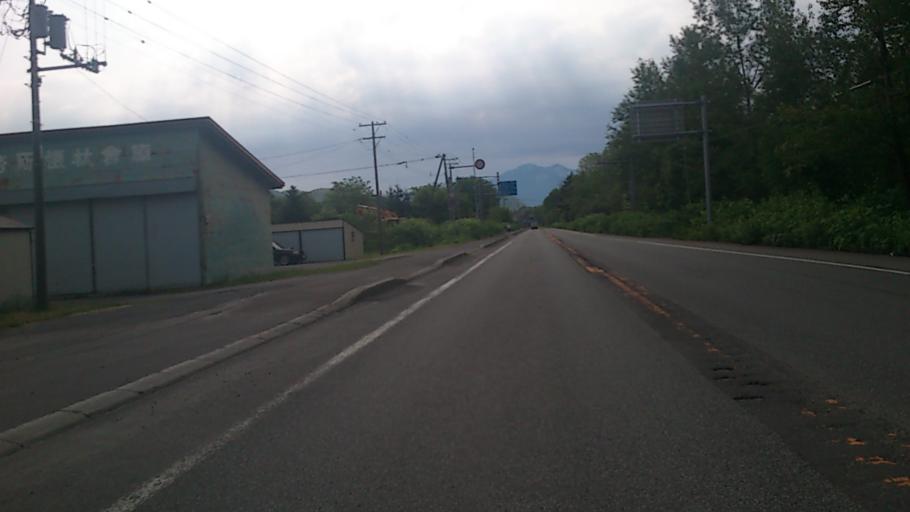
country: JP
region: Hokkaido
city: Kamikawa
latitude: 43.8458
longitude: 142.7589
